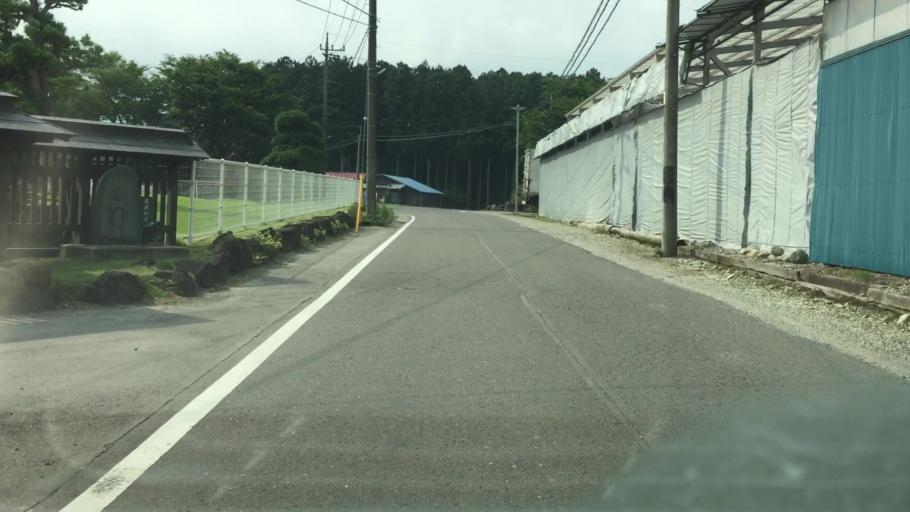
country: JP
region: Tochigi
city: Kuroiso
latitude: 36.9621
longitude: 139.9514
